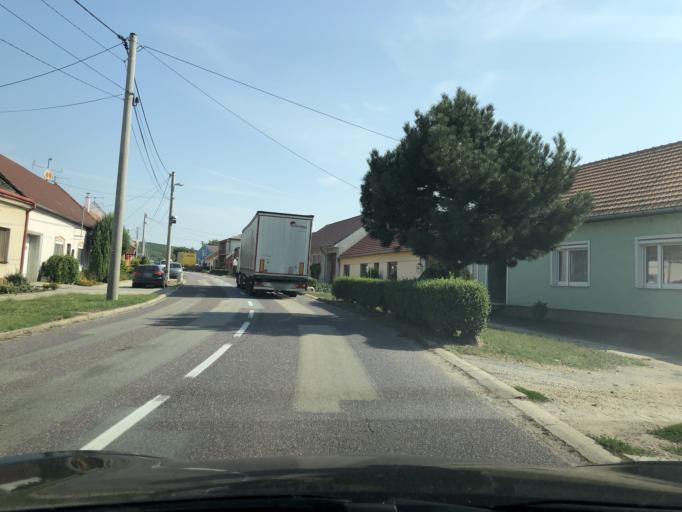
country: CZ
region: South Moravian
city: Brezi
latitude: 48.8195
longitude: 16.5681
